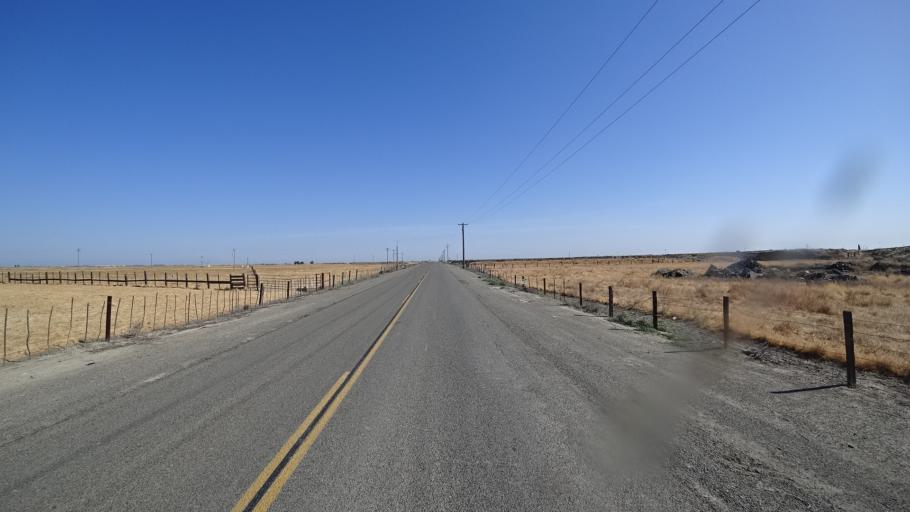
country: US
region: California
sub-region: Kings County
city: Corcoran
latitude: 36.1632
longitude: -119.5649
